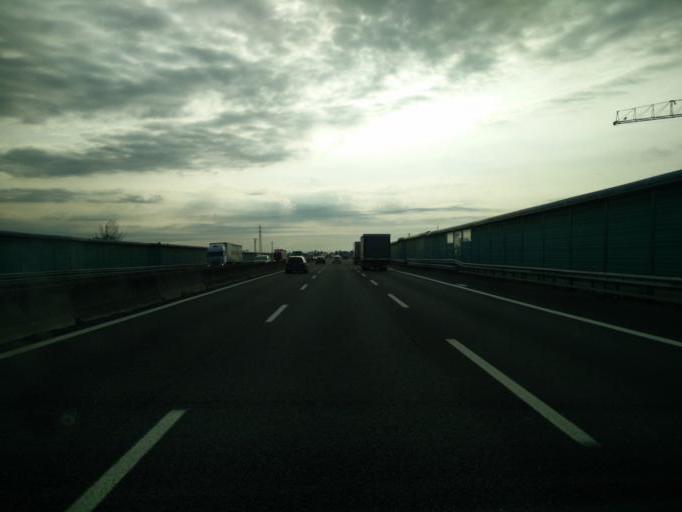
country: IT
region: Lombardy
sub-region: Provincia di Brescia
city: Castegnato
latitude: 45.5521
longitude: 10.1093
